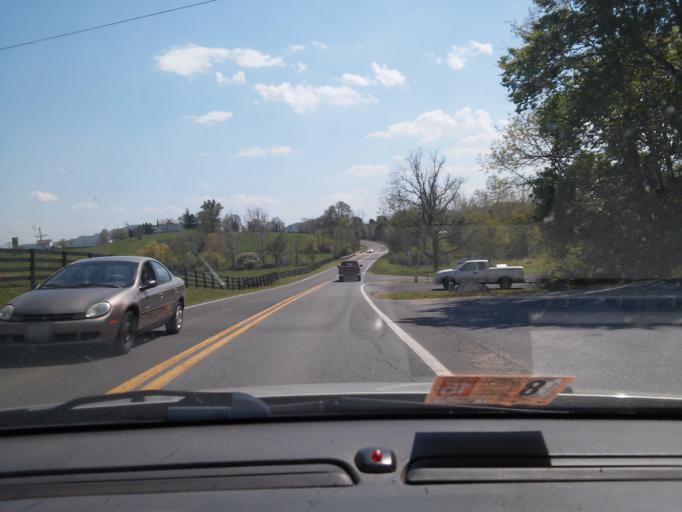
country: US
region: Virginia
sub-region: Rappahannock County
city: Washington
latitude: 38.7923
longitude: -78.1044
